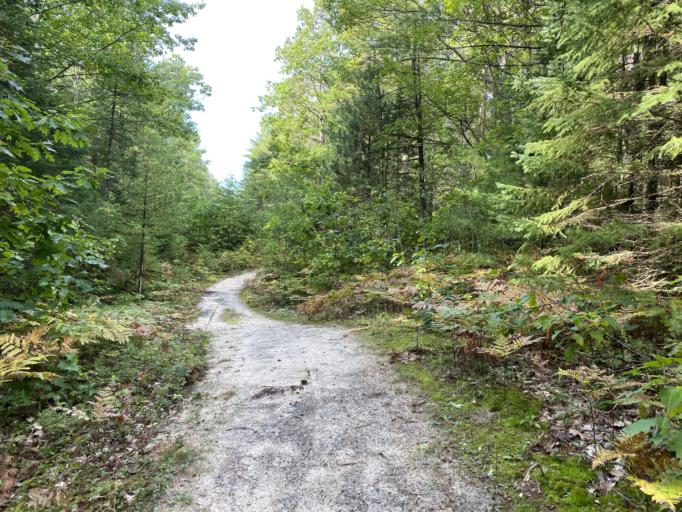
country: US
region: Michigan
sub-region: Mackinac County
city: Saint Ignace
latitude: 45.7486
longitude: -84.8872
